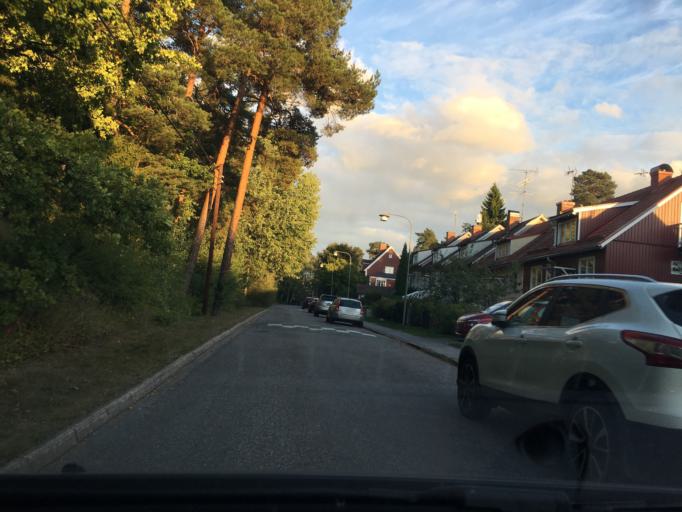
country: SE
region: Stockholm
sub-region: Stockholms Kommun
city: Bromma
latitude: 59.3279
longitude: 17.9642
